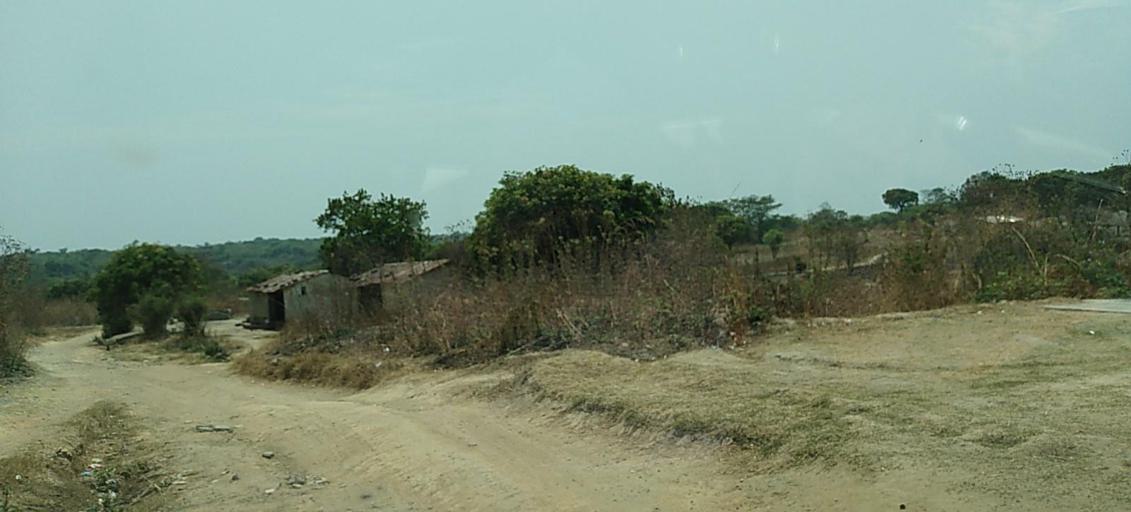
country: ZM
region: Copperbelt
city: Kalulushi
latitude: -12.9578
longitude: 28.1472
